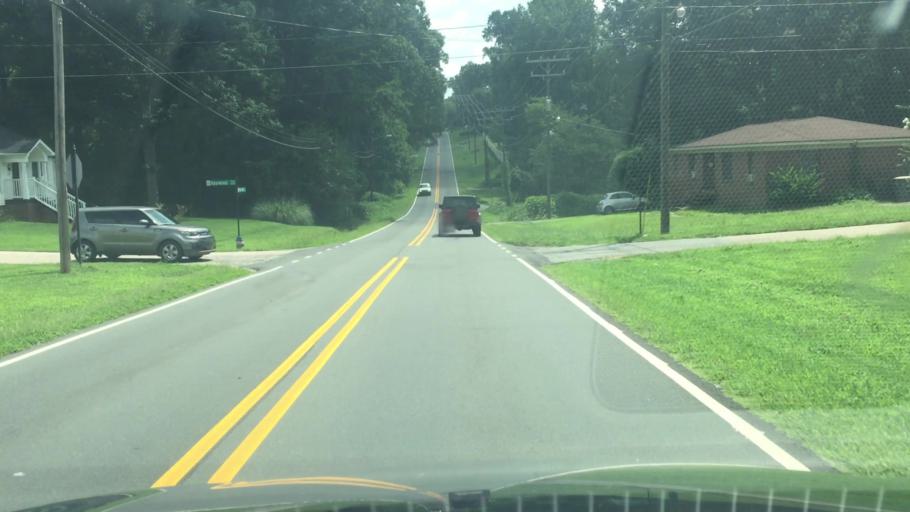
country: US
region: North Carolina
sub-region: Cabarrus County
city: Kannapolis
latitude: 35.4753
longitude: -80.6356
